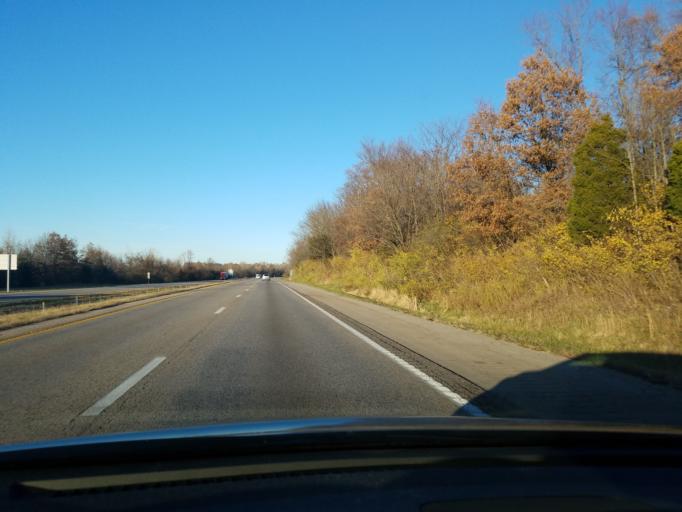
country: US
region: Missouri
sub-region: Franklin County
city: Saint Clair
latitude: 38.3736
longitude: -90.9715
